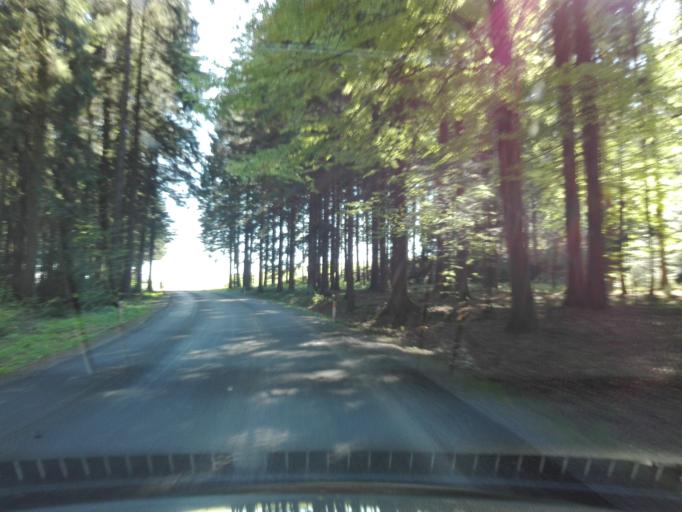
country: DE
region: Bavaria
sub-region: Lower Bavaria
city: Obernzell
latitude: 48.4462
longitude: 13.6763
